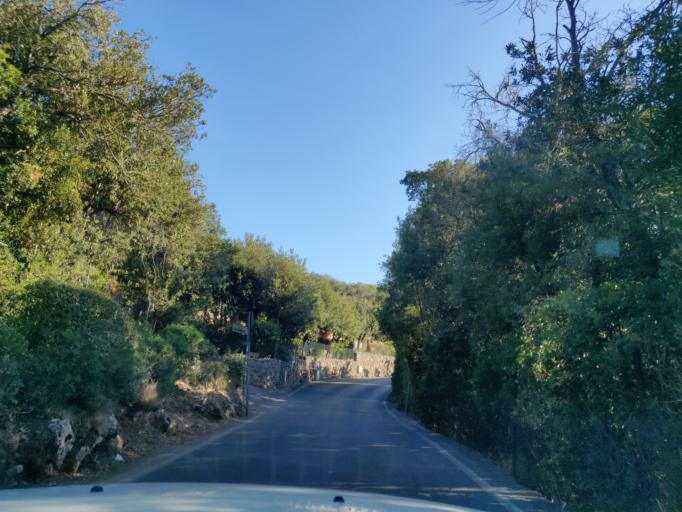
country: IT
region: Tuscany
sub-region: Provincia di Grosseto
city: Orbetello Scalo
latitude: 42.4166
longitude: 11.2826
